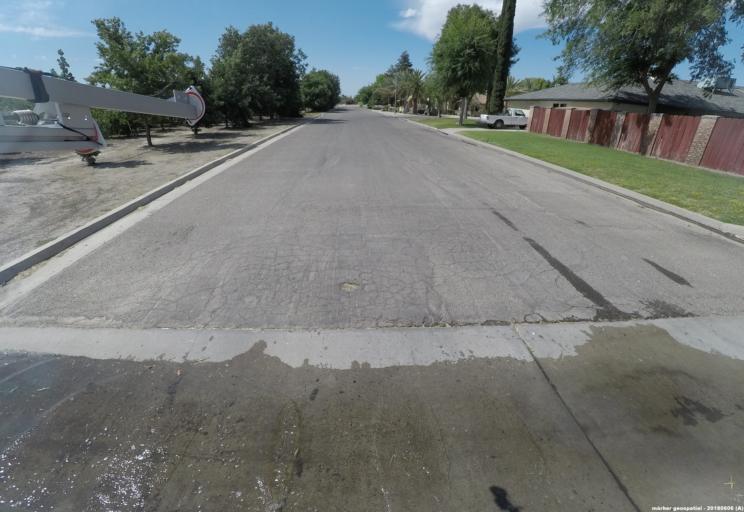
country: US
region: California
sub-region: Fresno County
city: Firebaugh
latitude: 36.8581
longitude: -120.4359
